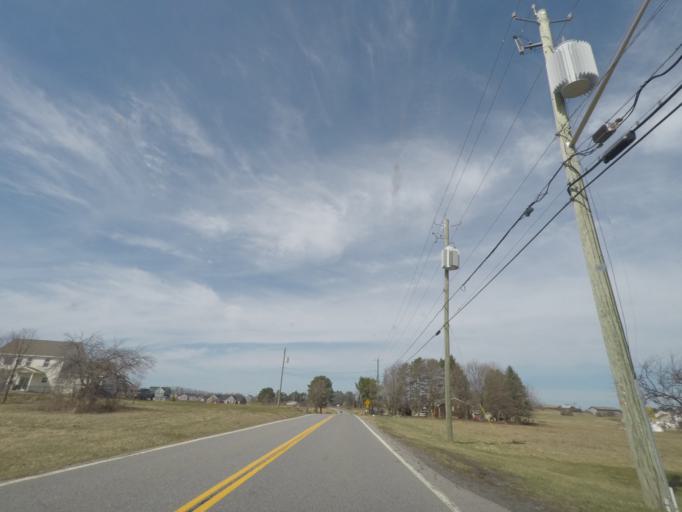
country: US
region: New York
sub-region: Saratoga County
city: Mechanicville
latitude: 42.9044
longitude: -73.7215
